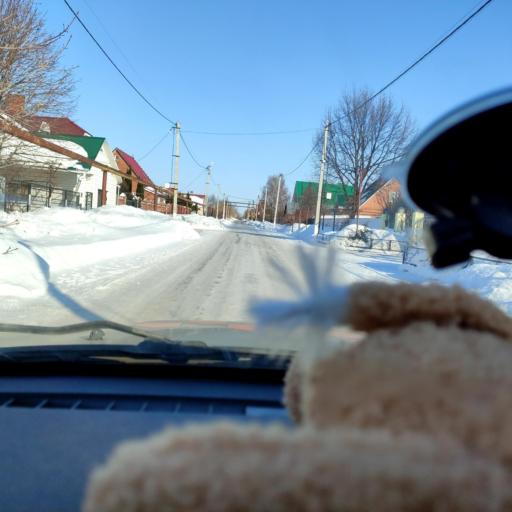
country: RU
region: Samara
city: Podstepki
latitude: 53.5147
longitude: 49.1204
